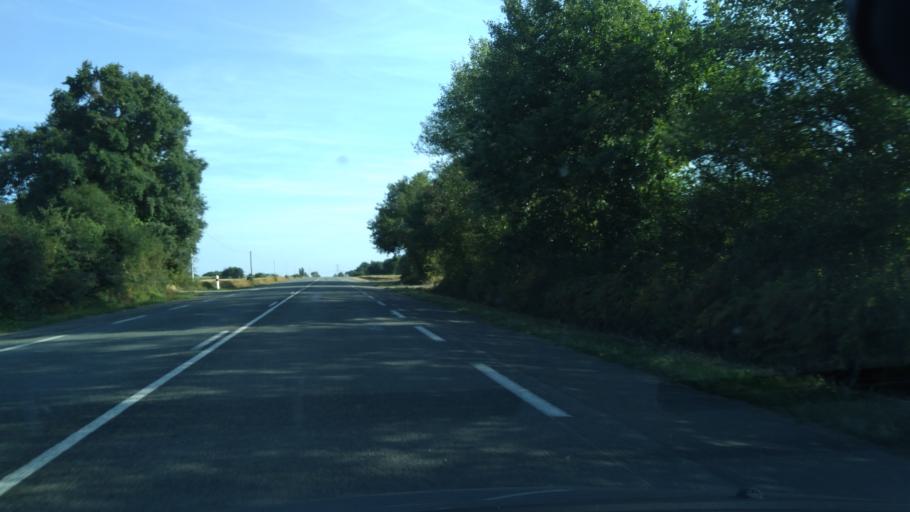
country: FR
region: Pays de la Loire
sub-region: Departement de la Mayenne
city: Entrammes
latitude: 47.9497
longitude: -0.7001
